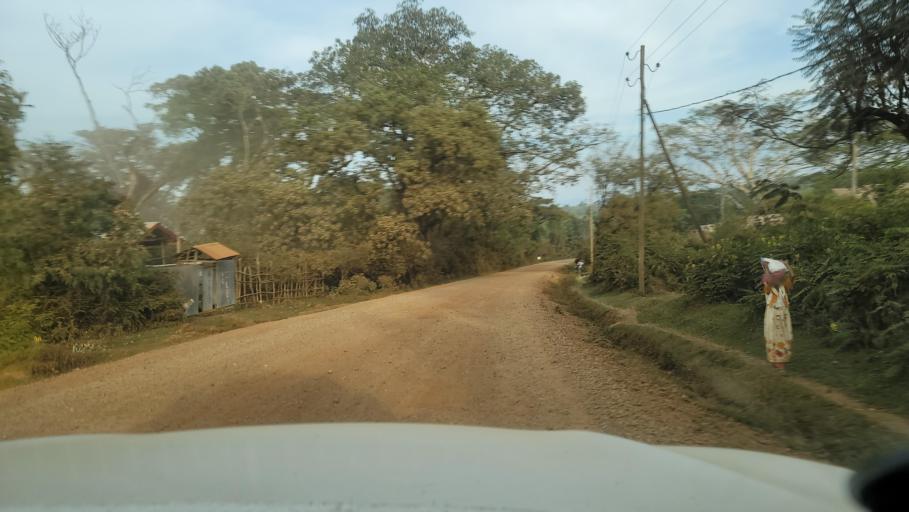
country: ET
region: Oromiya
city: Agaro
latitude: 7.8401
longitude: 36.5481
